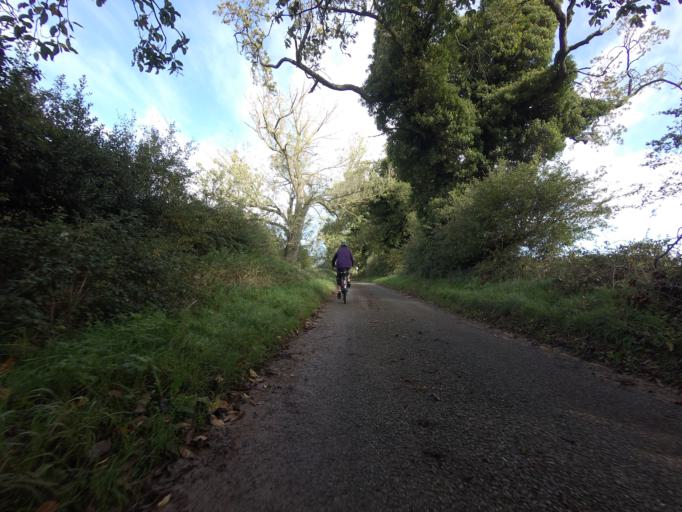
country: GB
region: England
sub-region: Norfolk
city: Dersingham
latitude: 52.8637
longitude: 0.6663
